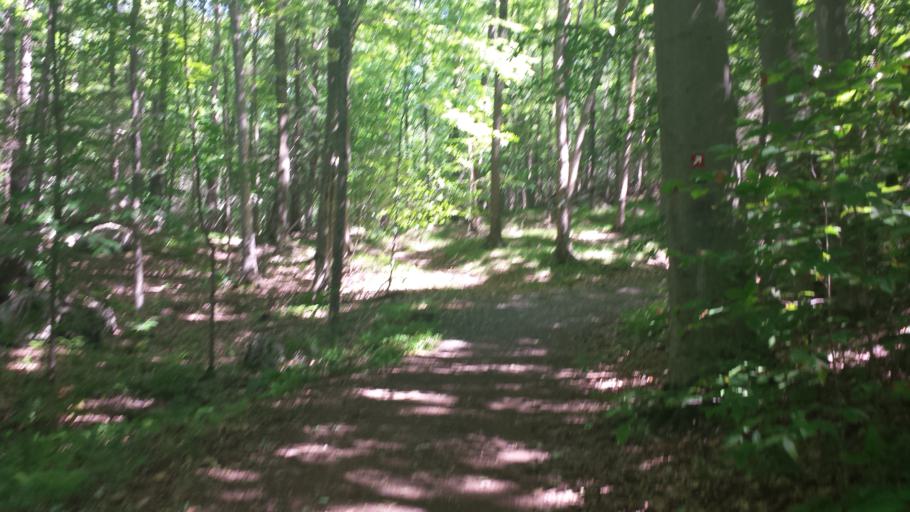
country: US
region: New York
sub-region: Westchester County
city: Pound Ridge
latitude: 41.2355
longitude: -73.5941
